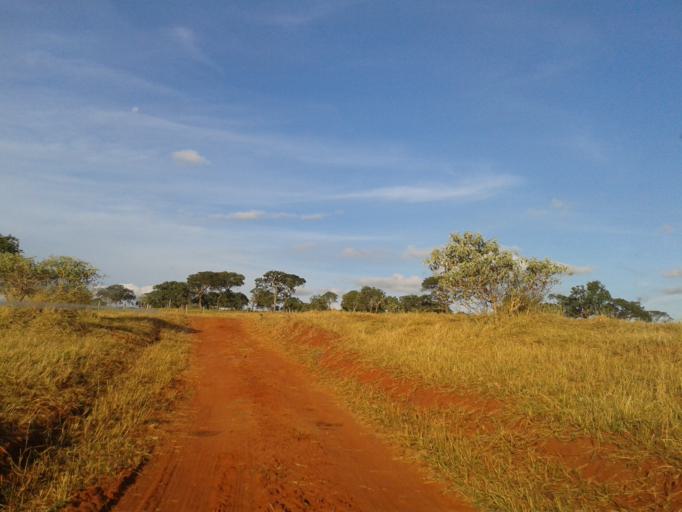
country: BR
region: Minas Gerais
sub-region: Campina Verde
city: Campina Verde
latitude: -19.4550
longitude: -49.6877
